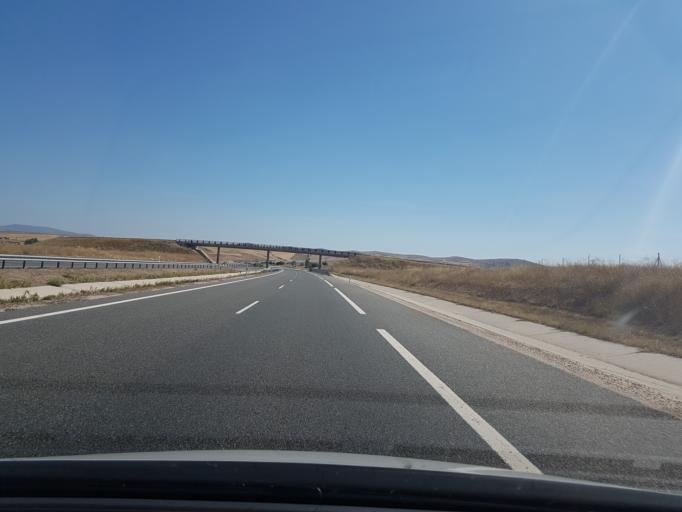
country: ES
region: Castille and Leon
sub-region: Provincia de Avila
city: Monsalupe
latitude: 40.8017
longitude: -4.7838
